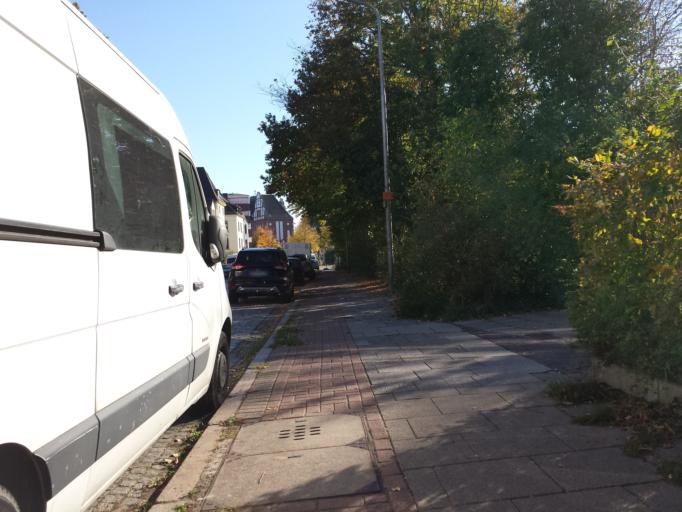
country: DE
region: Bremen
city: Bremen
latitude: 53.0991
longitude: 8.7801
